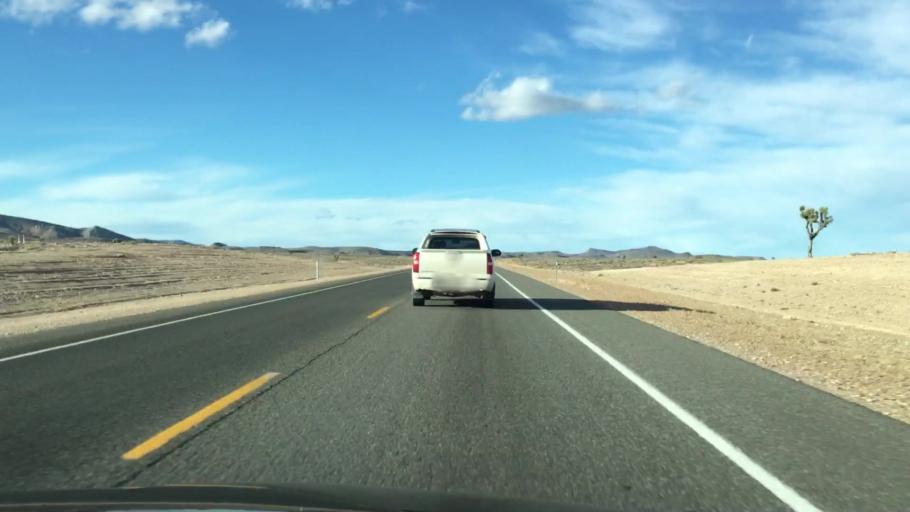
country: US
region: Nevada
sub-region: Esmeralda County
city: Goldfield
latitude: 37.5802
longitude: -117.2049
